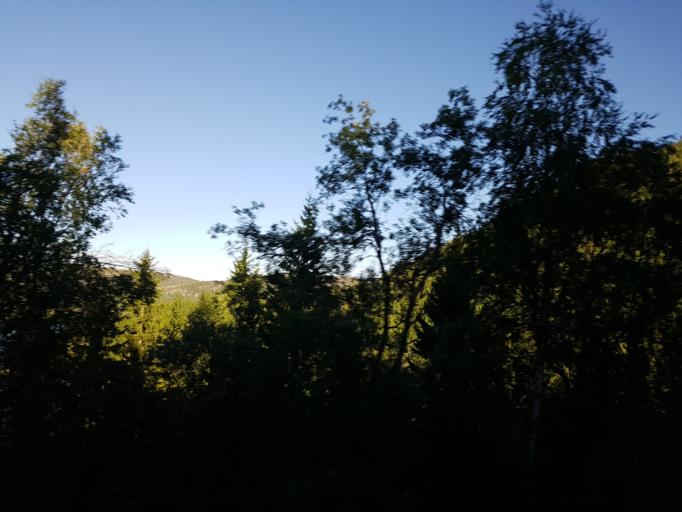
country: NO
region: Sor-Trondelag
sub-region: Afjord
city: A i Afjord
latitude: 63.7763
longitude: 10.2341
